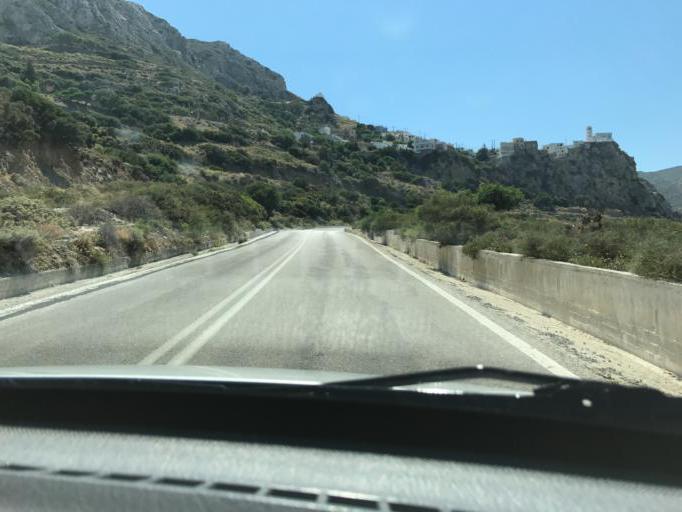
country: GR
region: South Aegean
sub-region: Nomos Dodekanisou
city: Karpathos
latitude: 35.4905
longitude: 27.1742
